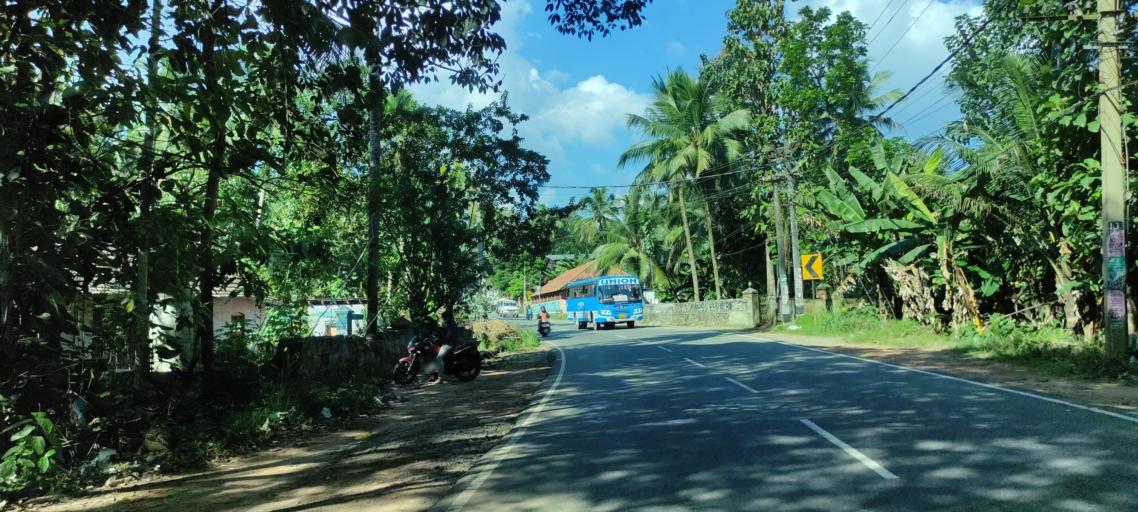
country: IN
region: Kerala
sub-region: Pattanamtitta
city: Pathanamthitta
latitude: 9.2336
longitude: 76.7553
